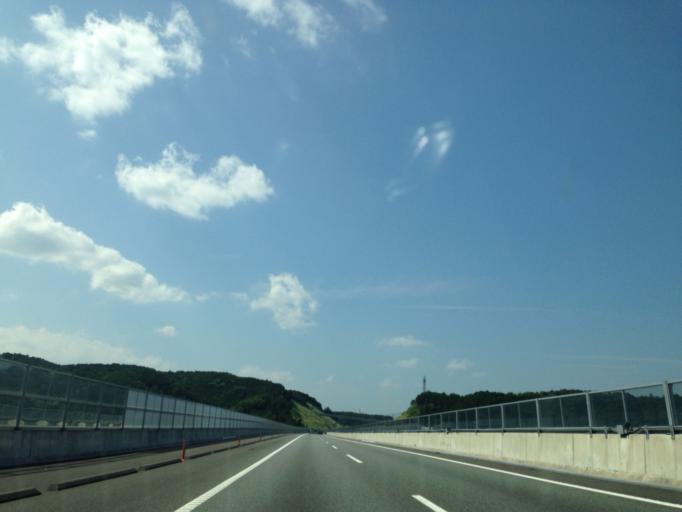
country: JP
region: Shizuoka
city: Mishima
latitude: 35.2018
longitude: 138.8877
